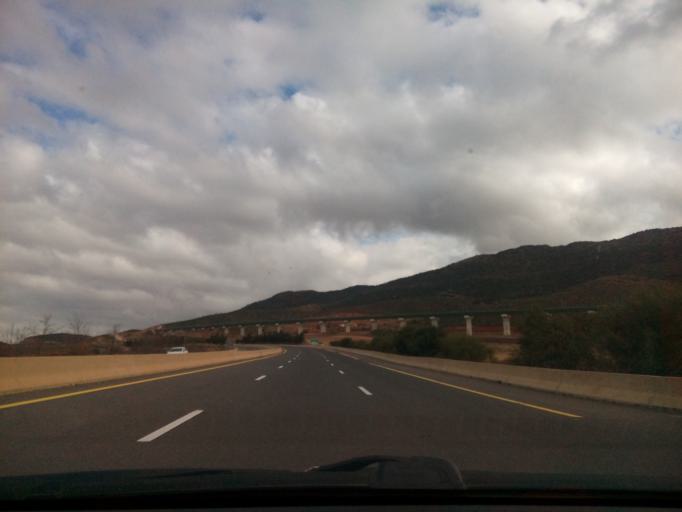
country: DZ
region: Tlemcen
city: Sidi Abdelli
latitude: 35.0094
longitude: -1.1674
